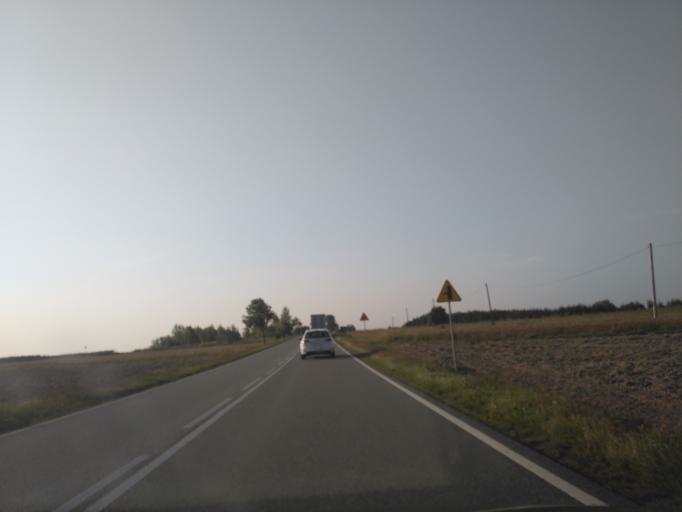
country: PL
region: Lublin Voivodeship
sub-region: Powiat janowski
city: Modliborzyce
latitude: 50.7847
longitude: 22.3217
